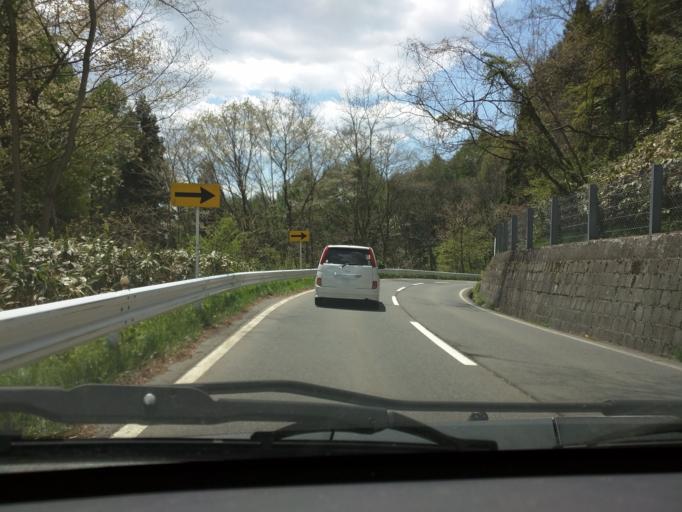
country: JP
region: Nagano
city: Nagano-shi
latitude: 36.6957
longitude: 138.1543
